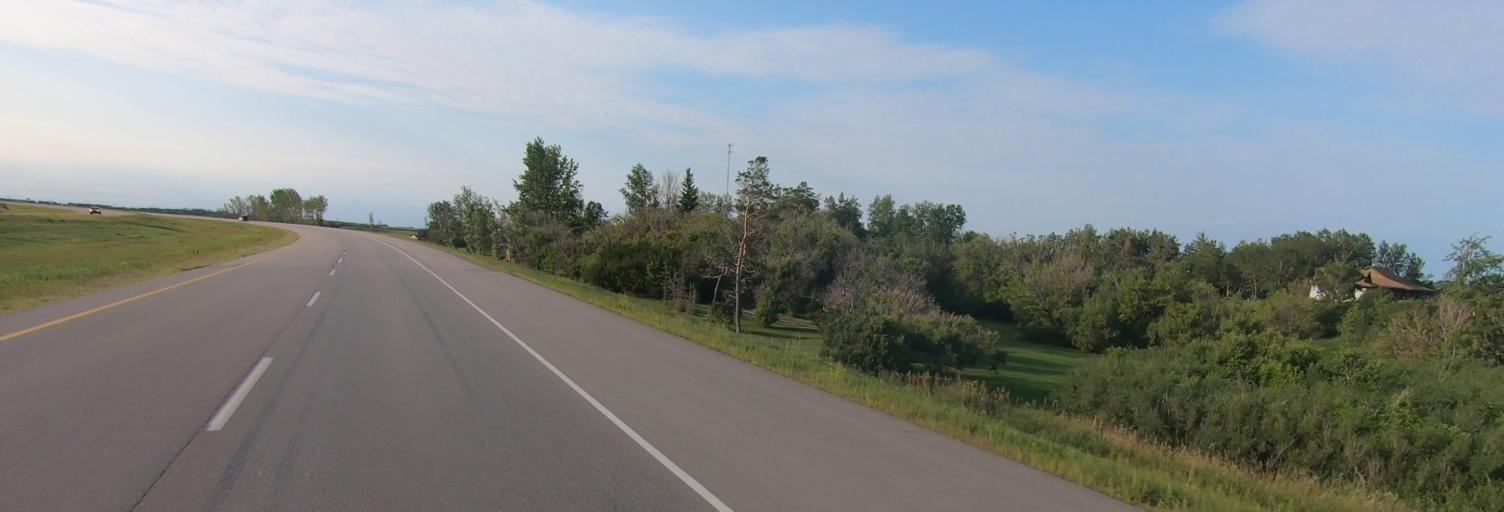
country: CA
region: Saskatchewan
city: Indian Head
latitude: 50.4243
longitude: -103.2871
